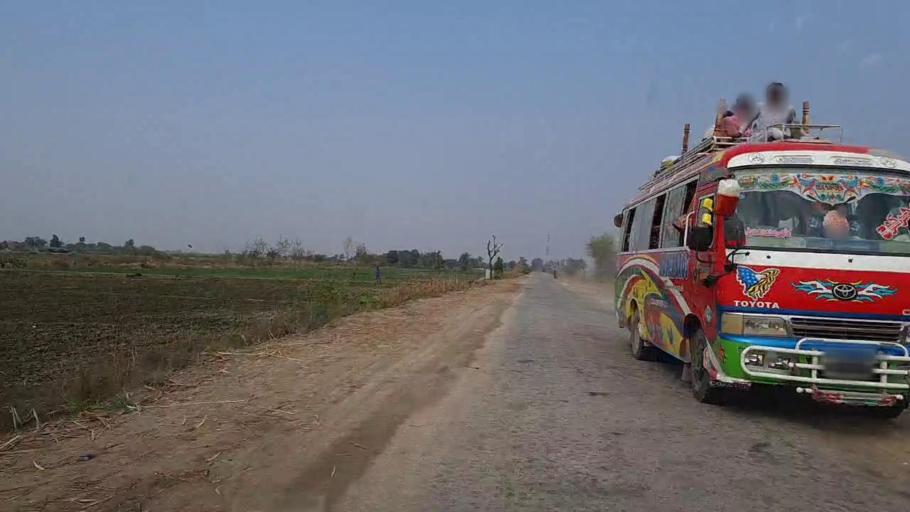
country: PK
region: Sindh
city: Mirwah Gorchani
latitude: 25.4213
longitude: 69.1493
